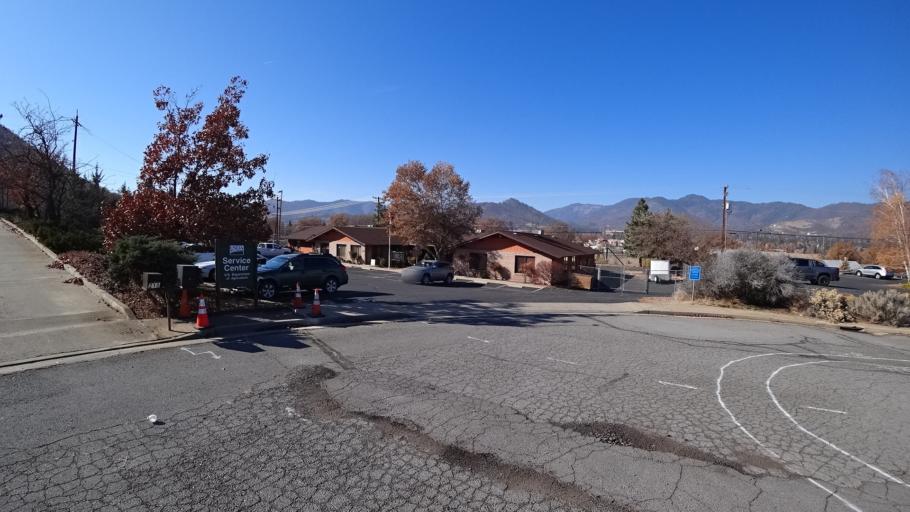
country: US
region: California
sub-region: Siskiyou County
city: Yreka
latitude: 41.7295
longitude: -122.6307
